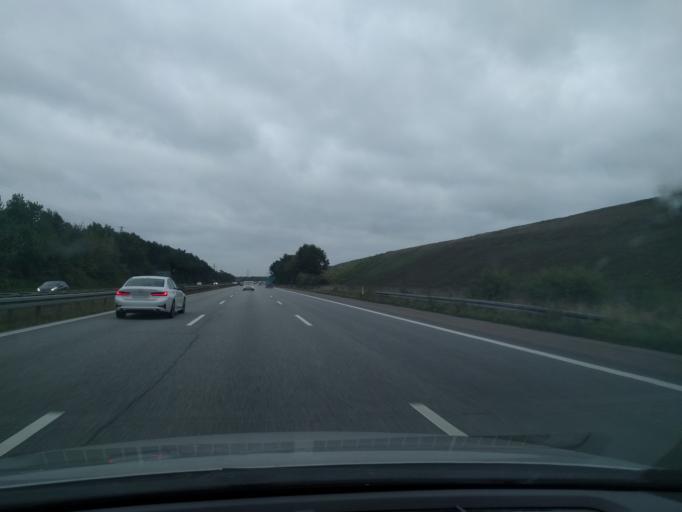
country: DK
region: Capital Region
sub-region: Ishoj Kommune
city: Ishoj
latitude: 55.6197
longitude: 12.3548
